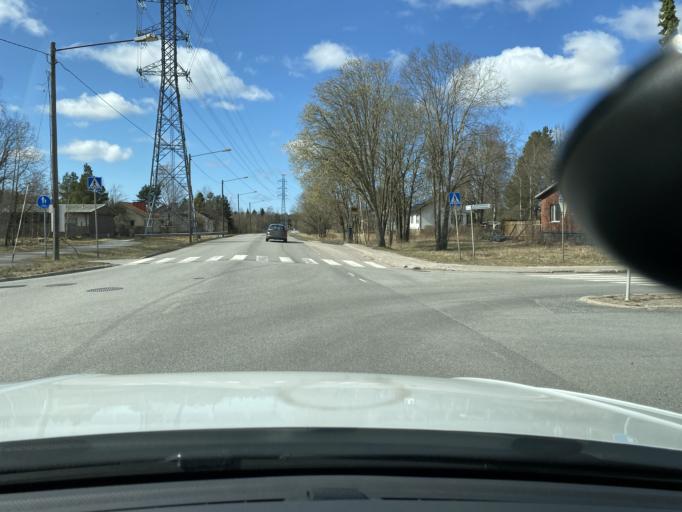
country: FI
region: Varsinais-Suomi
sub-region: Turku
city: Turku
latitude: 60.4751
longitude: 22.2739
